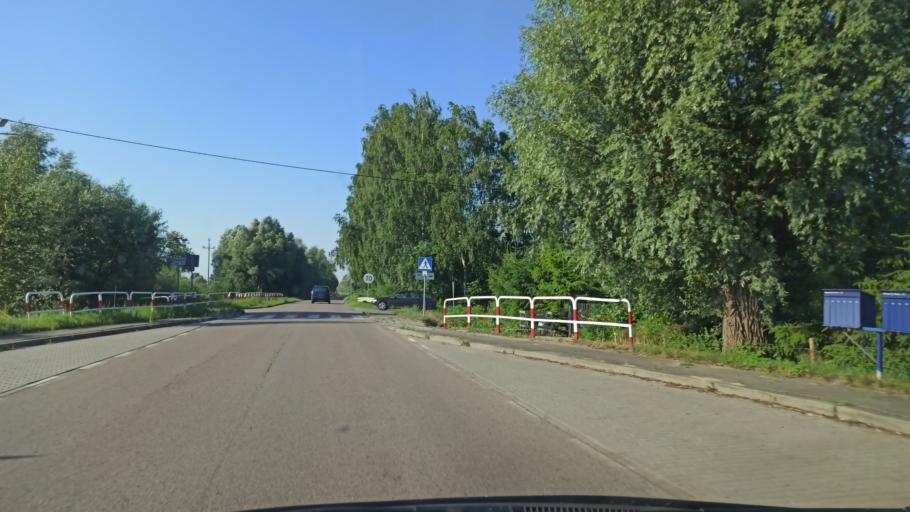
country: PL
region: Warmian-Masurian Voivodeship
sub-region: Powiat elblaski
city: Elblag
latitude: 54.1745
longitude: 19.3314
